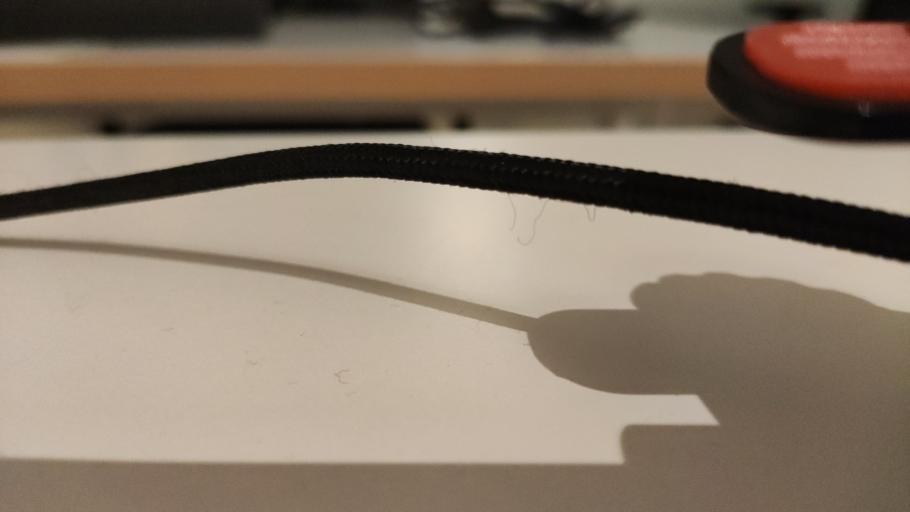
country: RU
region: Moskovskaya
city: Kurovskoye
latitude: 55.5873
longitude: 38.9033
